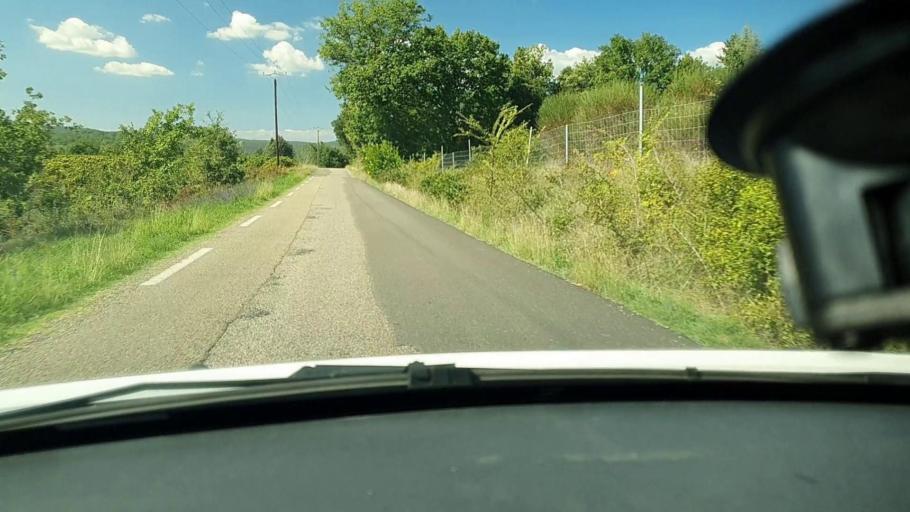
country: FR
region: Languedoc-Roussillon
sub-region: Departement du Gard
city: Goudargues
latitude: 44.1782
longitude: 4.4933
